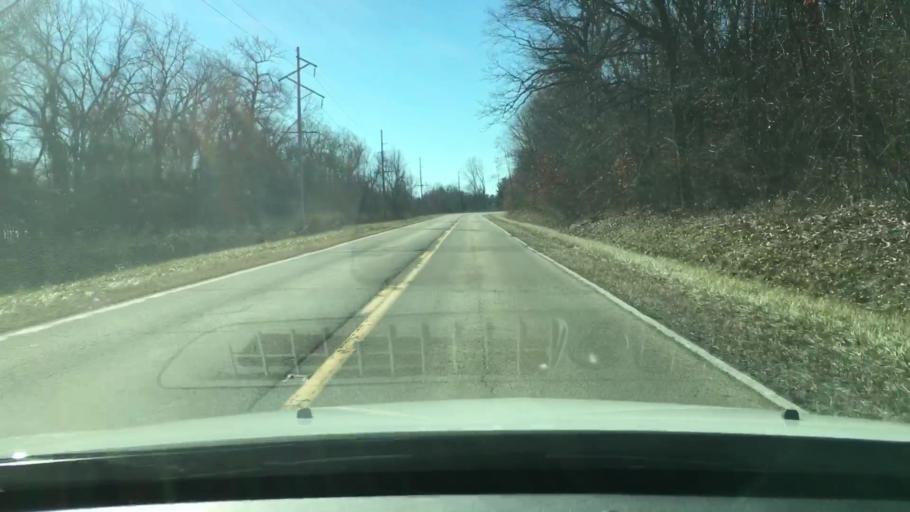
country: US
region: Illinois
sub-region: Fulton County
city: Astoria
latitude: 40.1892
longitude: -90.2088
